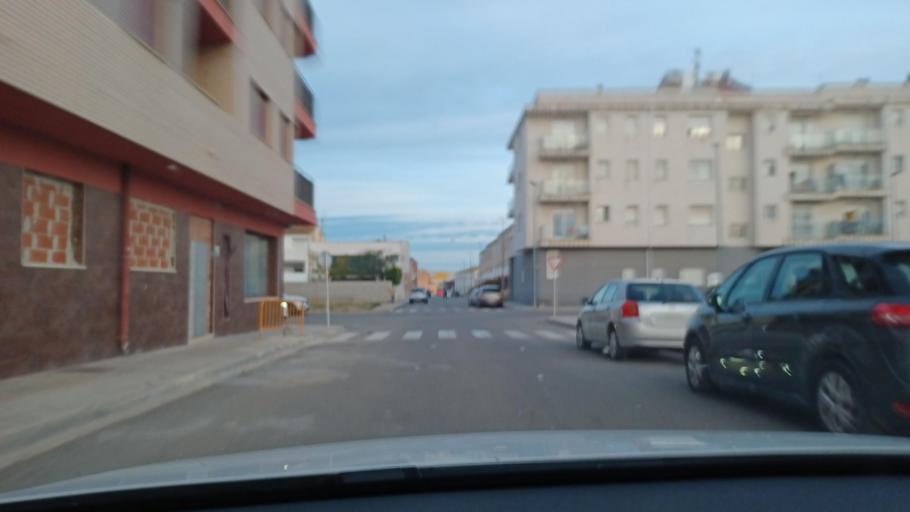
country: ES
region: Catalonia
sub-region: Provincia de Tarragona
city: Amposta
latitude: 40.7022
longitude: 0.5745
